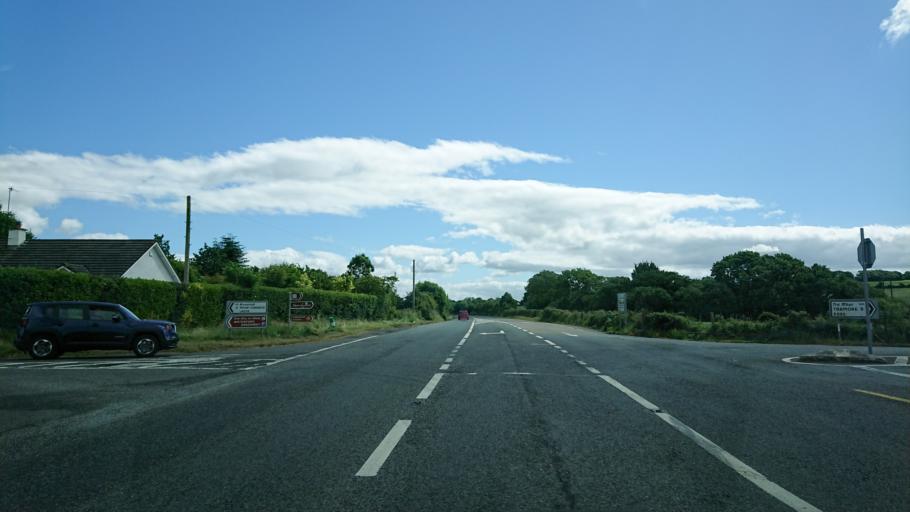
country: IE
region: Leinster
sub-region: Kilkenny
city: Mooncoin
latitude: 52.2317
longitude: -7.2008
